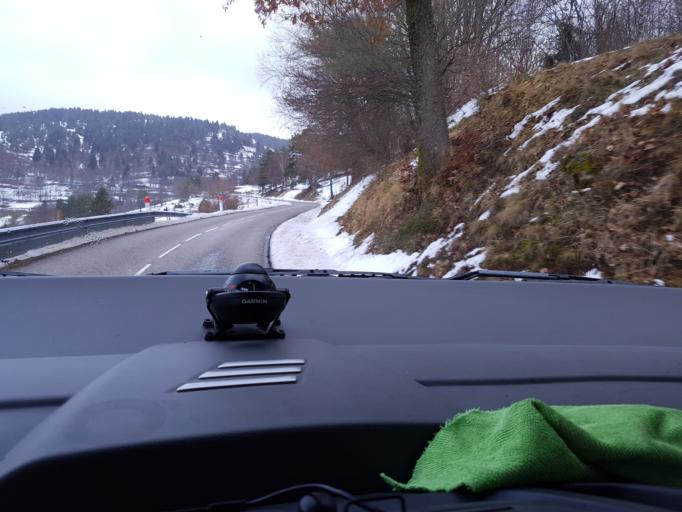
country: FR
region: Alsace
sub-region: Departement du Haut-Rhin
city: Soultzeren
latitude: 48.0763
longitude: 7.1037
